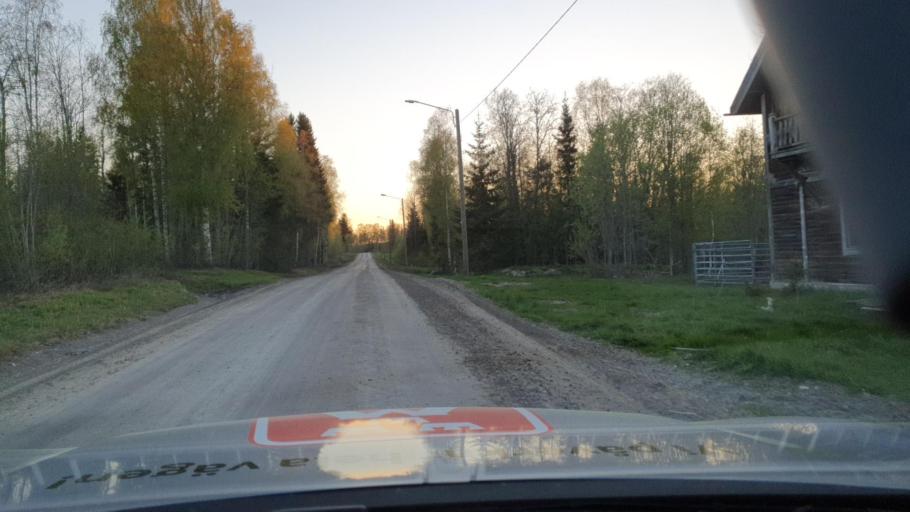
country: SE
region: Vaesternorrland
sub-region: OErnskoeldsviks Kommun
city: Bjasta
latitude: 63.5054
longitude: 18.4776
